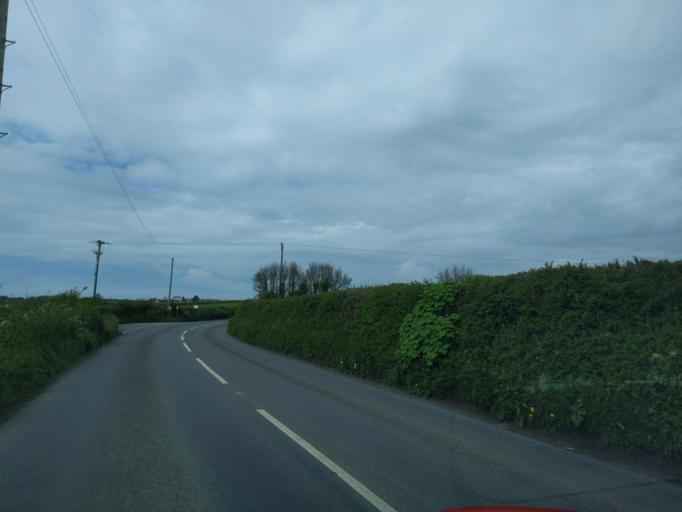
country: GB
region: England
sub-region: Cornwall
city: Wadebridge
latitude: 50.5428
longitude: -4.8622
